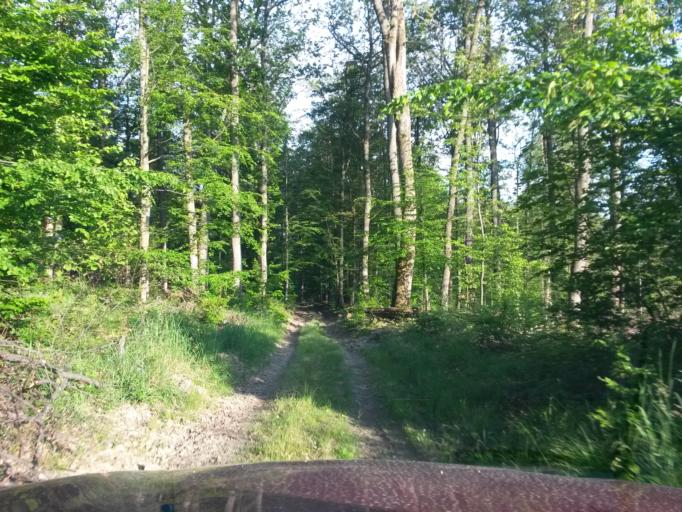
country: SK
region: Kosicky
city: Moldava nad Bodvou
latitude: 48.7337
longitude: 21.0430
